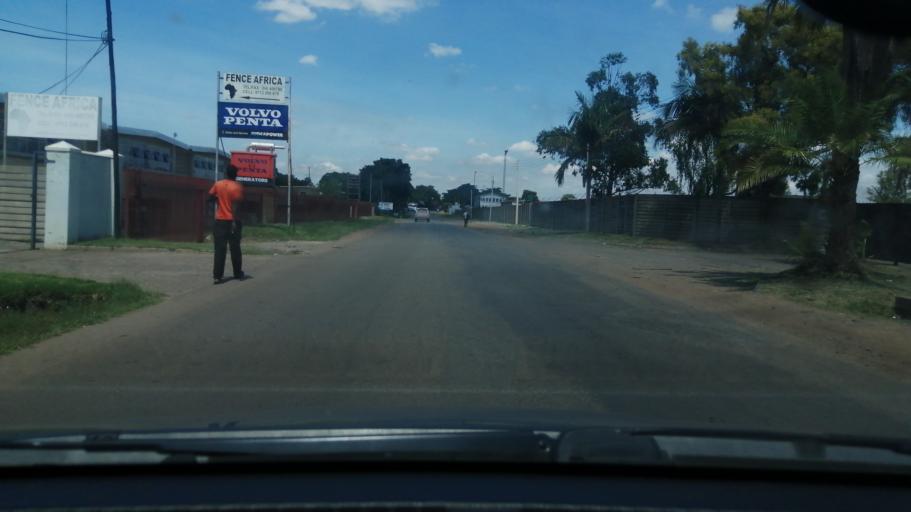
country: ZW
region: Harare
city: Epworth
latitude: -17.8445
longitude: 31.1168
